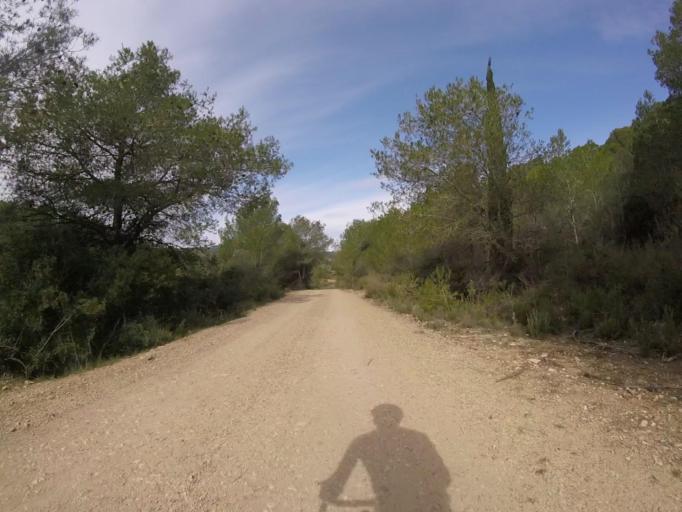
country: ES
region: Valencia
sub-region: Provincia de Castello
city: Torreblanca
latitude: 40.2039
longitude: 0.1433
